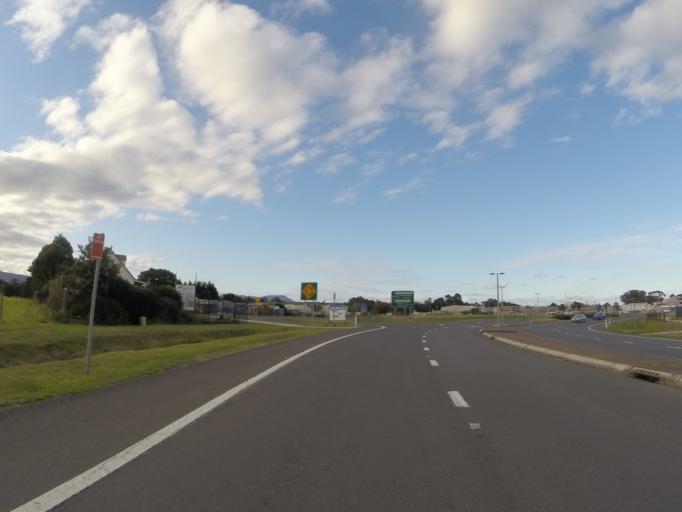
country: AU
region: New South Wales
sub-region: Shellharbour
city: Albion Park Rail
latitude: -34.5499
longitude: 150.7839
